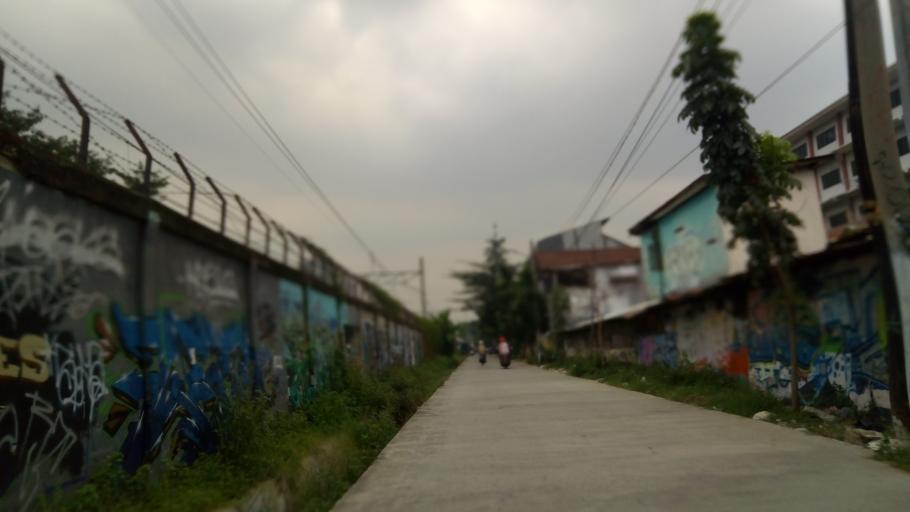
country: ID
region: Jakarta Raya
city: Jakarta
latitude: -6.1556
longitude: 106.8400
